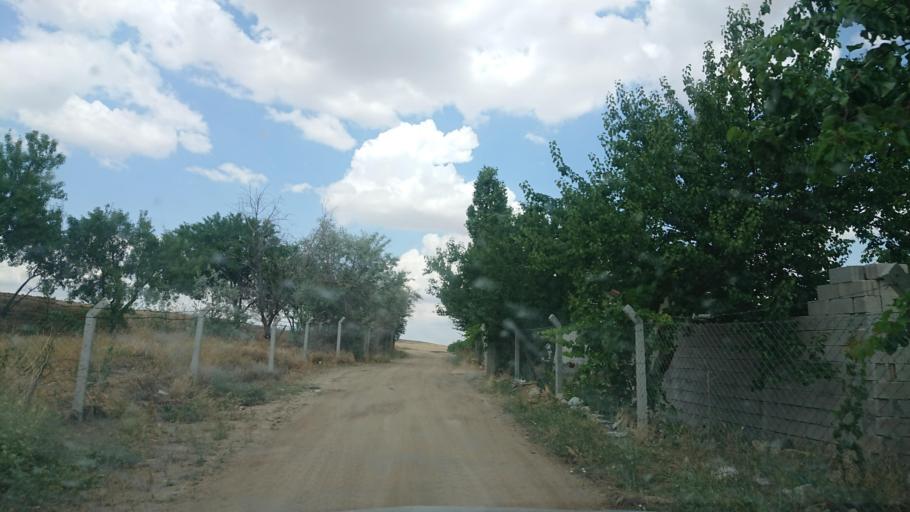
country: TR
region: Aksaray
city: Agacoren
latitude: 38.8921
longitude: 33.8826
